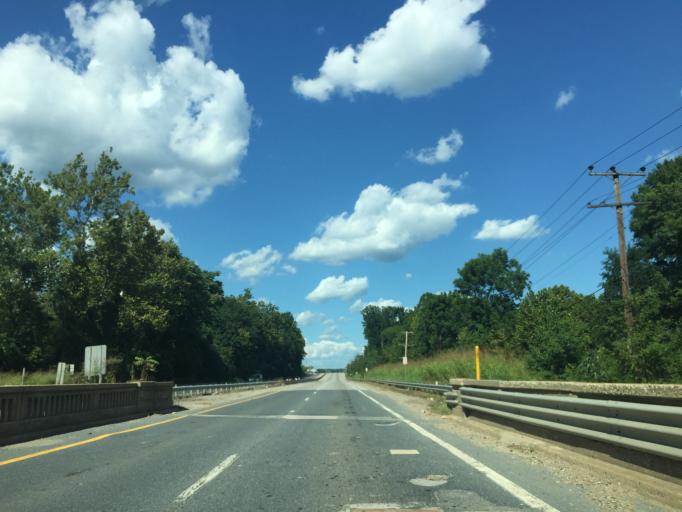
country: US
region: Maryland
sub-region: Baltimore County
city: Kingsville
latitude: 39.4088
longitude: -76.3899
